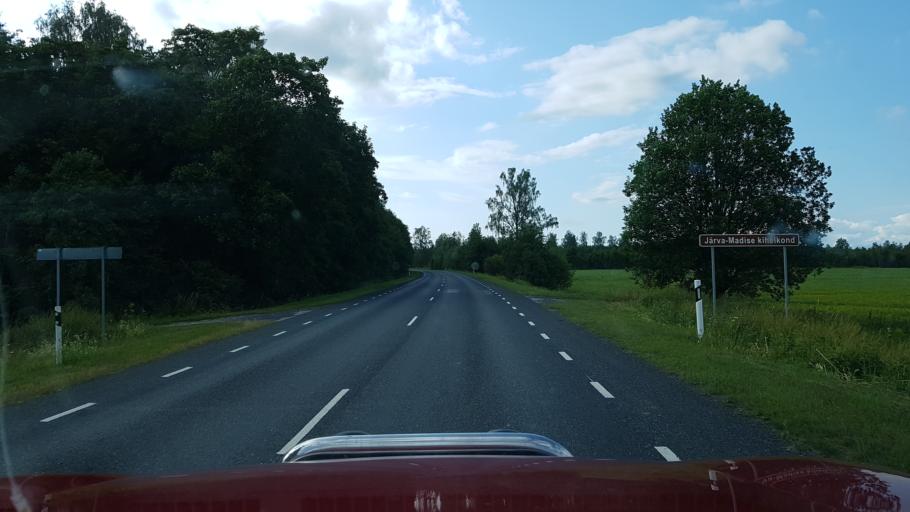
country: EE
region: Jaervamaa
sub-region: Jaerva-Jaani vald
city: Jarva-Jaani
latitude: 59.1012
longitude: 25.8157
